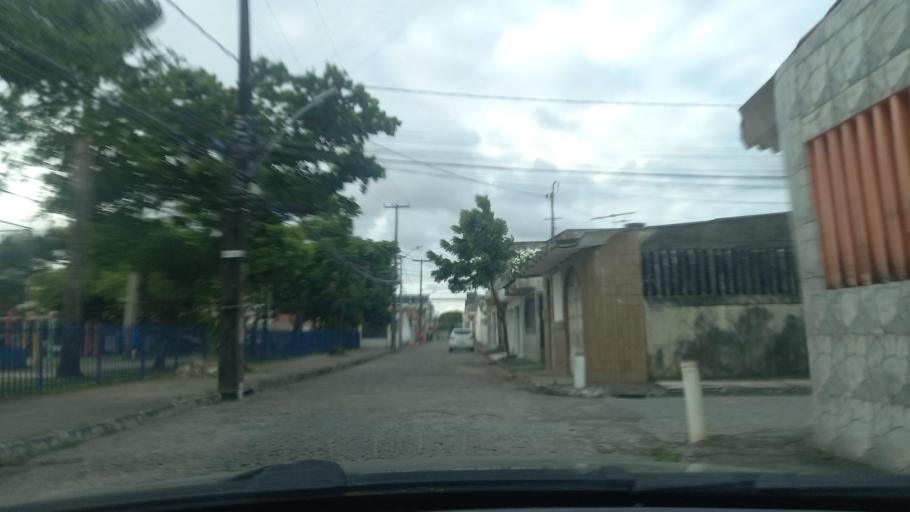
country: BR
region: Pernambuco
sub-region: Recife
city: Recife
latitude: -8.1159
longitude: -34.9181
